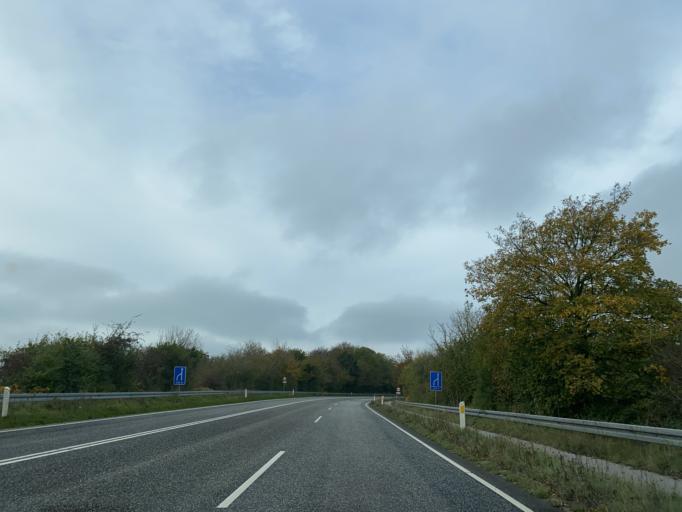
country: DK
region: South Denmark
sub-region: Aabenraa Kommune
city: Aabenraa
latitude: 55.0647
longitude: 9.4321
